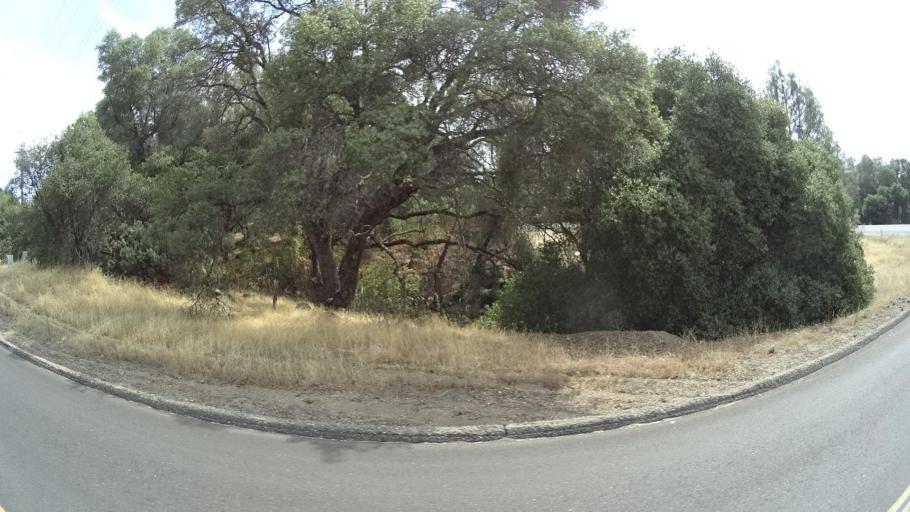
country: US
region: California
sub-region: Mariposa County
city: Mariposa
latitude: 37.4606
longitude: -119.9016
